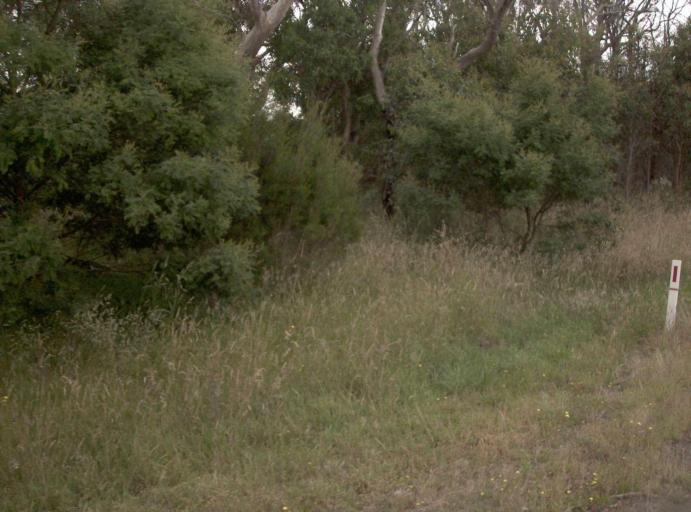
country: AU
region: Victoria
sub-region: Latrobe
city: Traralgon
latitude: -38.5572
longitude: 146.8105
